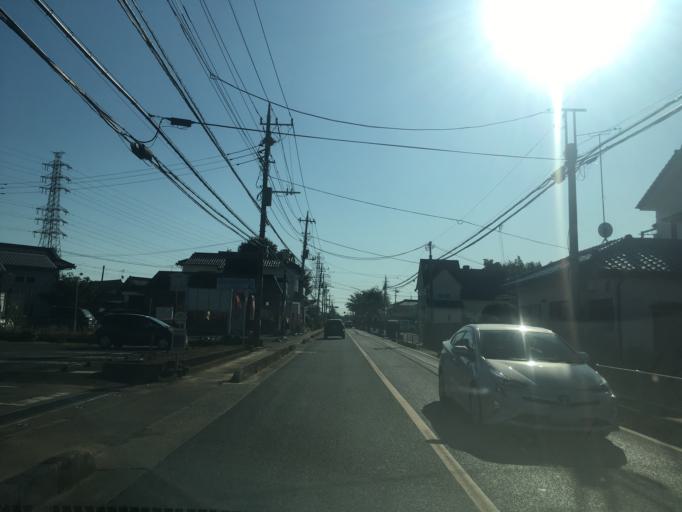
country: JP
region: Saitama
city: Kawagoe
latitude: 35.8710
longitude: 139.4730
